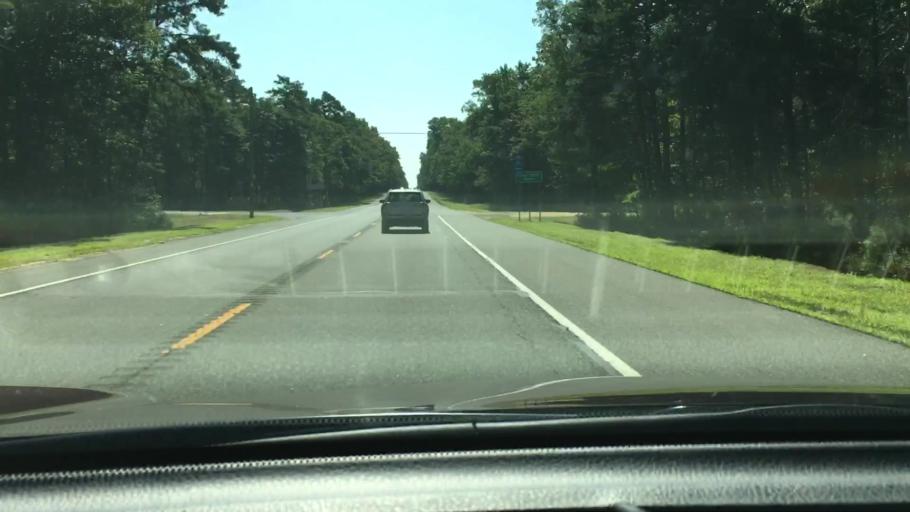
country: US
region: New Jersey
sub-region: Cumberland County
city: Laurel Lake
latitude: 39.3498
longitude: -74.9079
